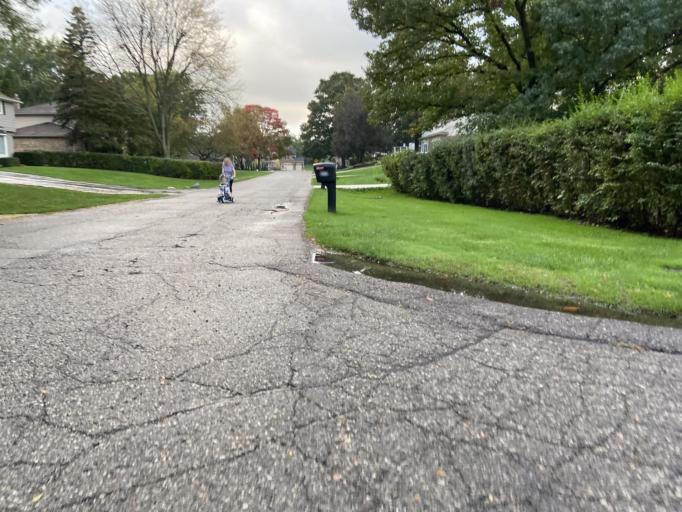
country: US
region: Michigan
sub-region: Oakland County
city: West Bloomfield Township
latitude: 42.5371
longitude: -83.3575
